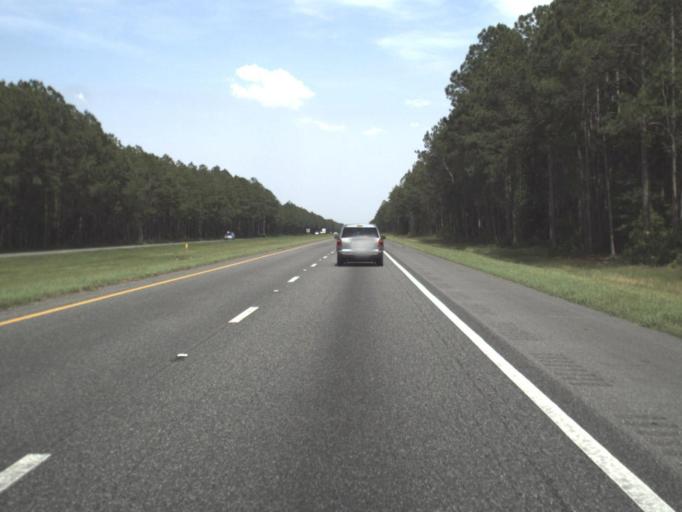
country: US
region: Florida
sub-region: Union County
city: Lake Butler
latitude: 30.2542
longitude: -82.3753
